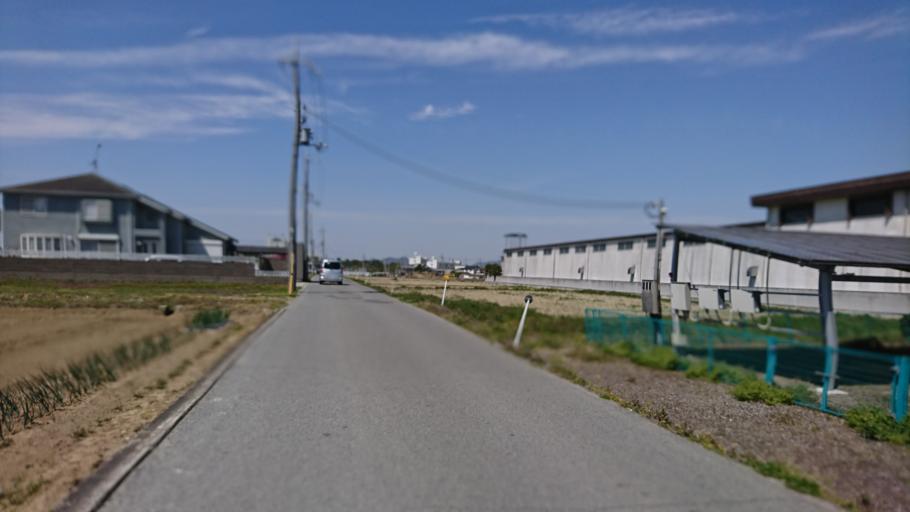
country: JP
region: Hyogo
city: Kakogawacho-honmachi
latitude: 34.7435
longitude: 134.8871
